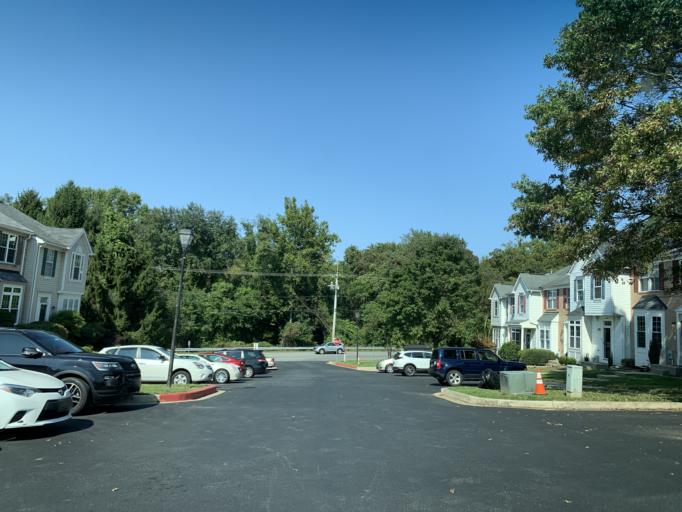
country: US
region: Maryland
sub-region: Harford County
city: Bel Air South
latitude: 39.4884
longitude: -76.3313
